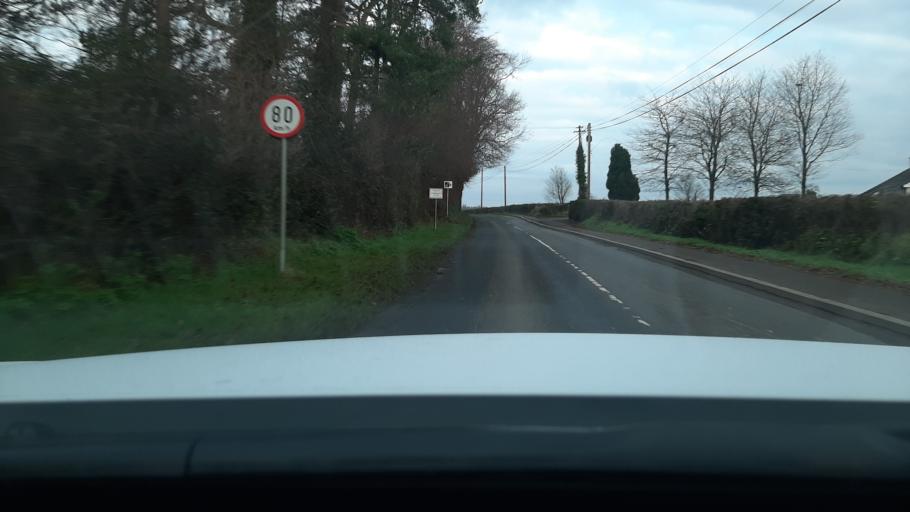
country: IE
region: Leinster
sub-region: Kildare
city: Rathangan
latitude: 53.2261
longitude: -7.0063
